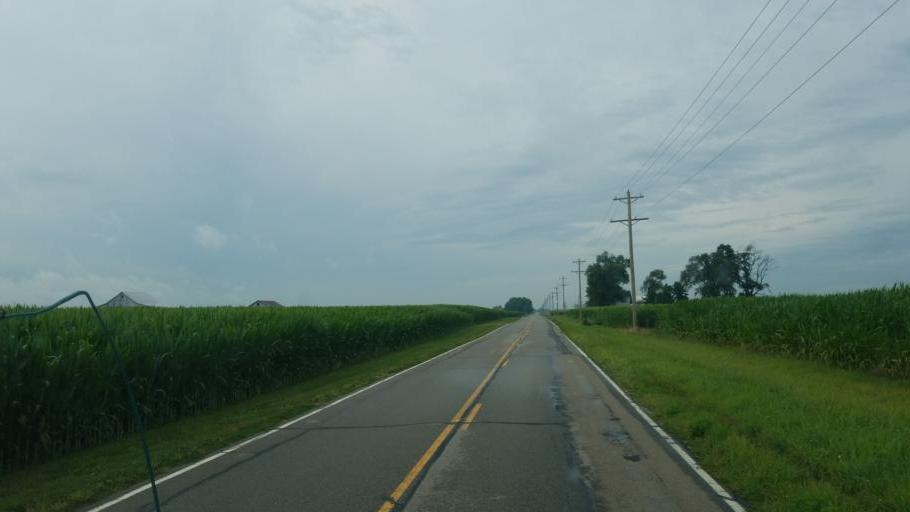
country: US
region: Ohio
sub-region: Defiance County
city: Hicksville
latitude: 41.3186
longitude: -84.6898
